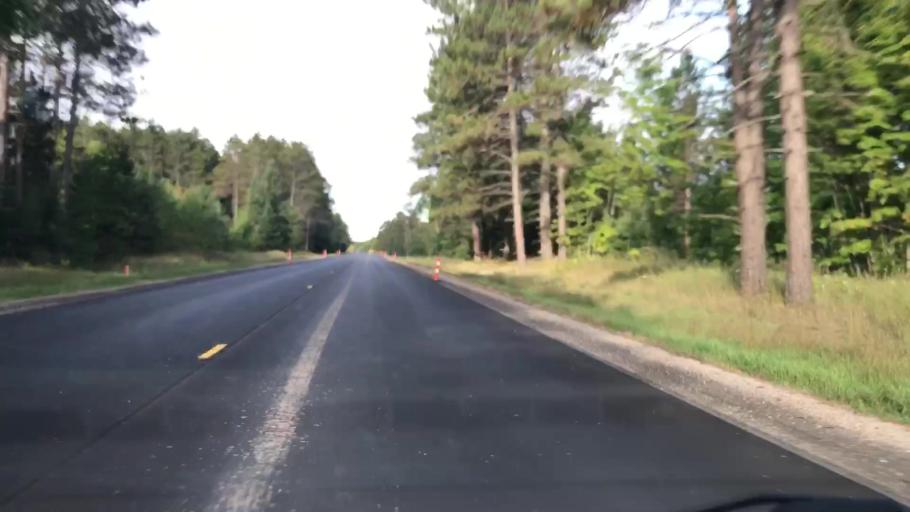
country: US
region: Michigan
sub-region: Luce County
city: Newberry
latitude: 46.3464
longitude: -85.0125
